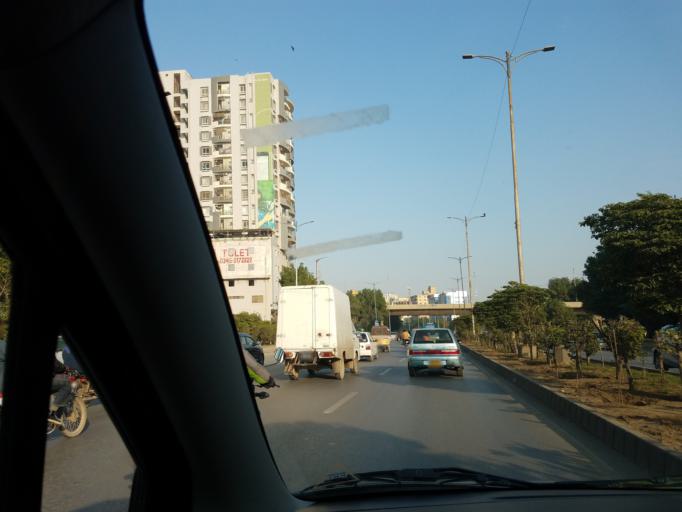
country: PK
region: Sindh
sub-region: Karachi District
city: Karachi
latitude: 24.8598
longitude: 67.0573
